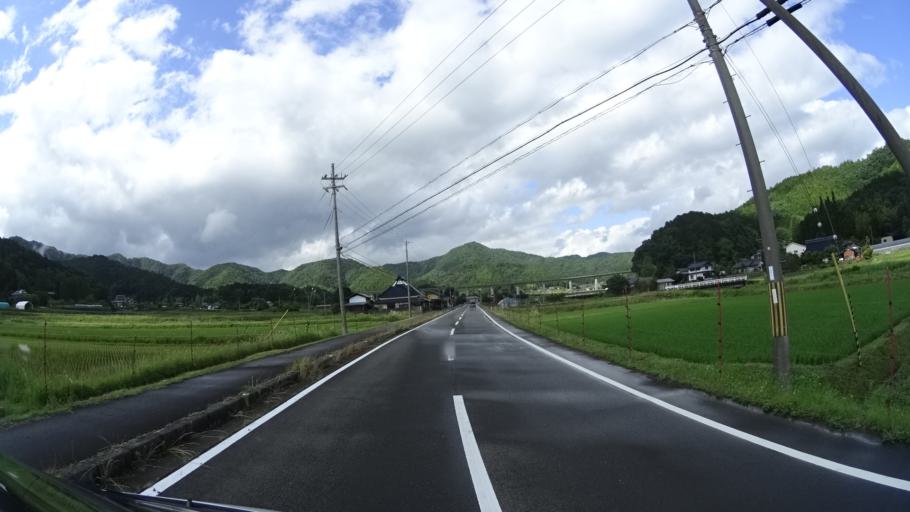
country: JP
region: Kyoto
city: Ayabe
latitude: 35.3806
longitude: 135.2386
